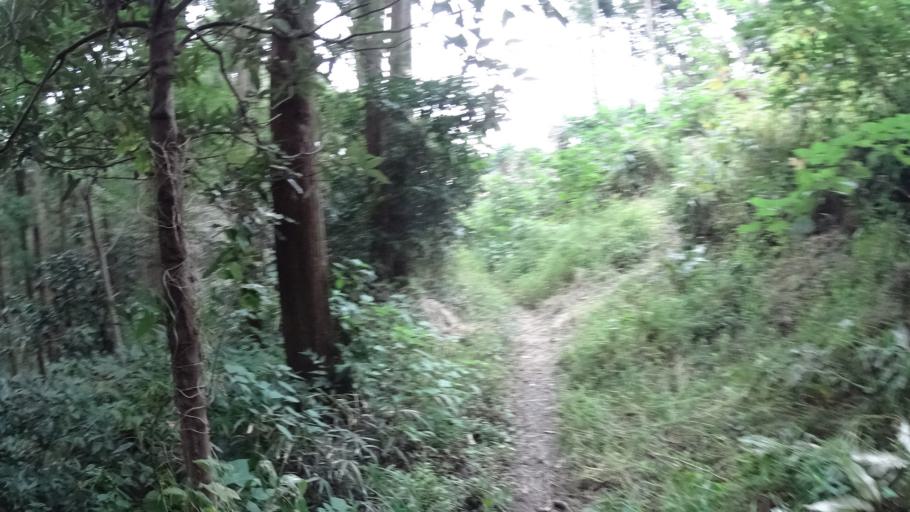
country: JP
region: Kanagawa
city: Zushi
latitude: 35.2853
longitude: 139.6216
